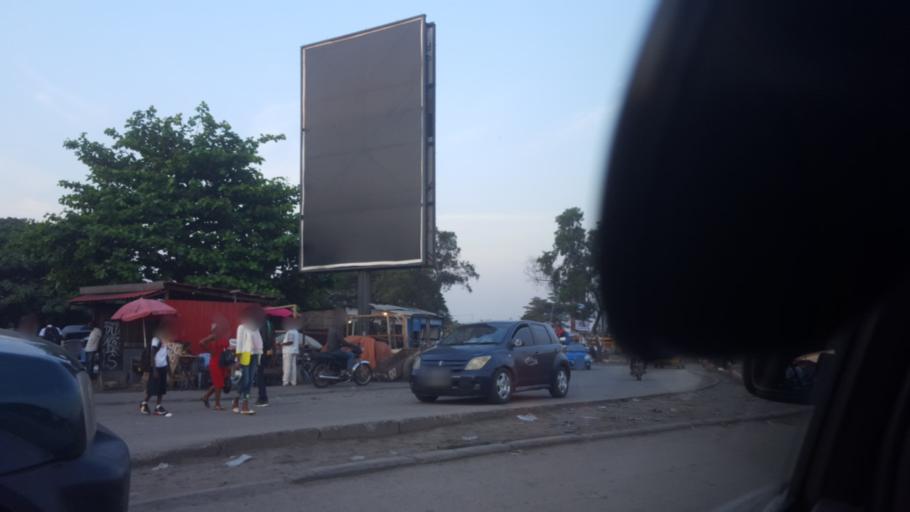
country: CD
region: Kinshasa
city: Kinshasa
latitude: -4.3442
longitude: 15.3241
